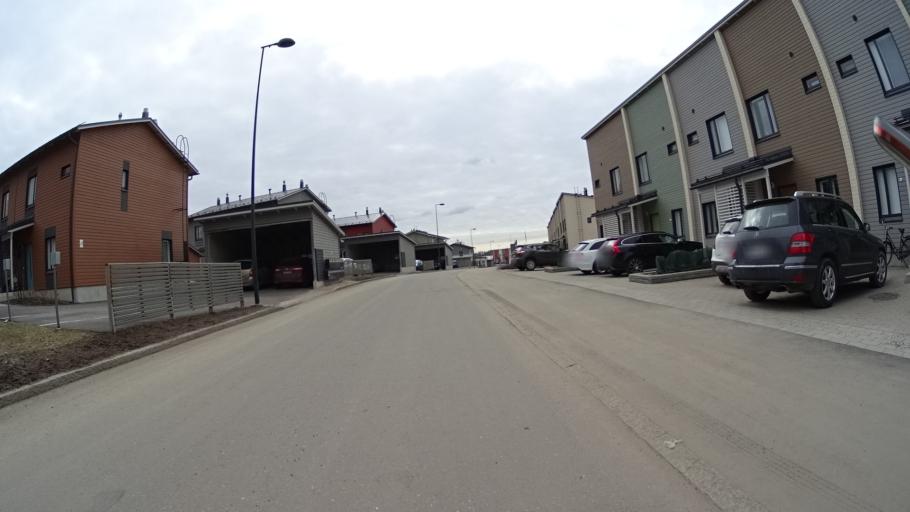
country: FI
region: Uusimaa
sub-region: Helsinki
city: Vantaa
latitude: 60.2932
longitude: 24.9407
